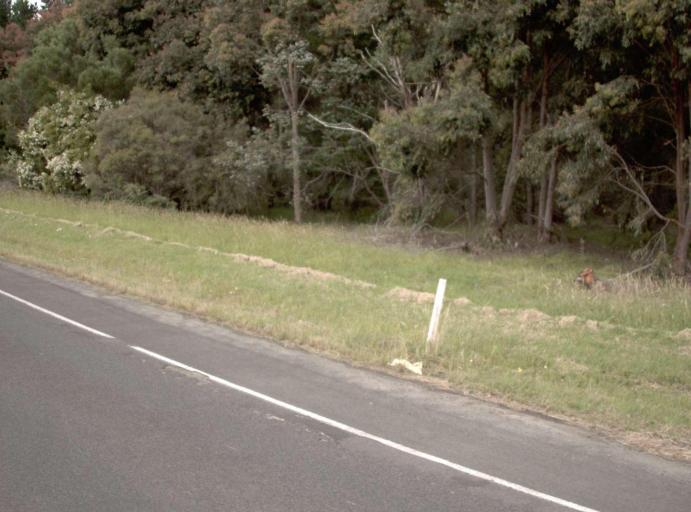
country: AU
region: Victoria
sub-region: Latrobe
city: Morwell
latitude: -38.1923
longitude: 146.4504
